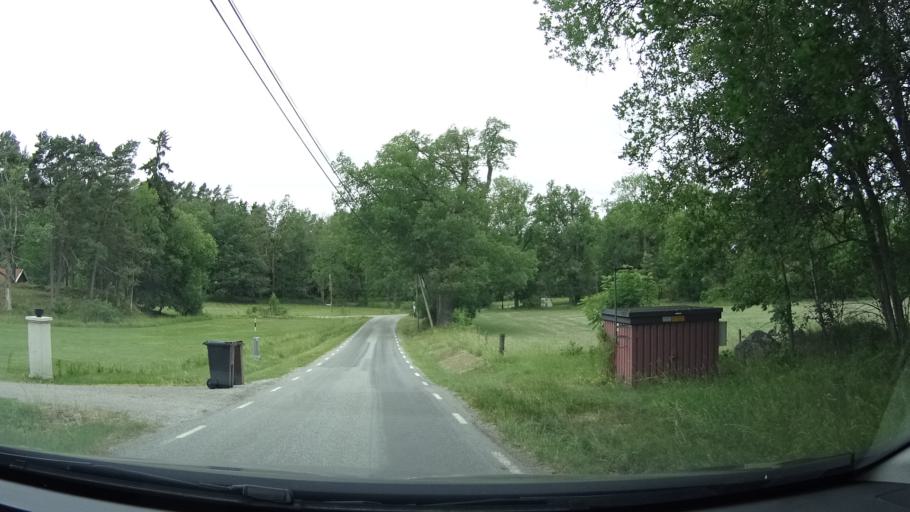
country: SE
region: Stockholm
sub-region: Varmdo Kommun
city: Mortnas
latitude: 59.3791
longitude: 18.4608
